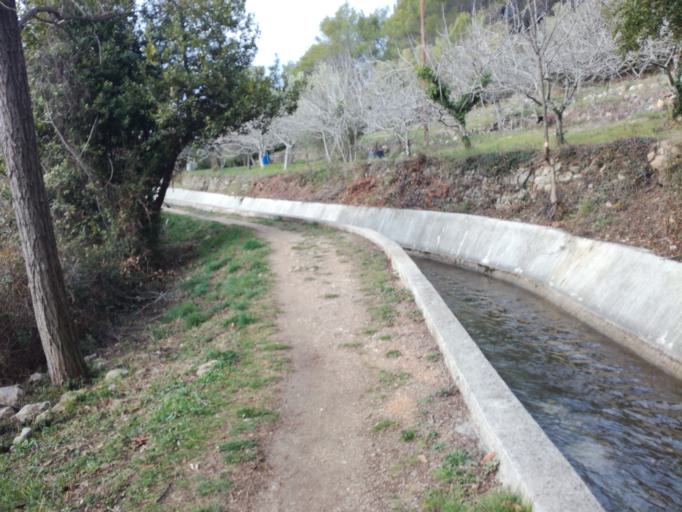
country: FR
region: Provence-Alpes-Cote d'Azur
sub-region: Departement des Alpes-Maritimes
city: Mouans-Sartoux
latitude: 43.6135
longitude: 6.9862
